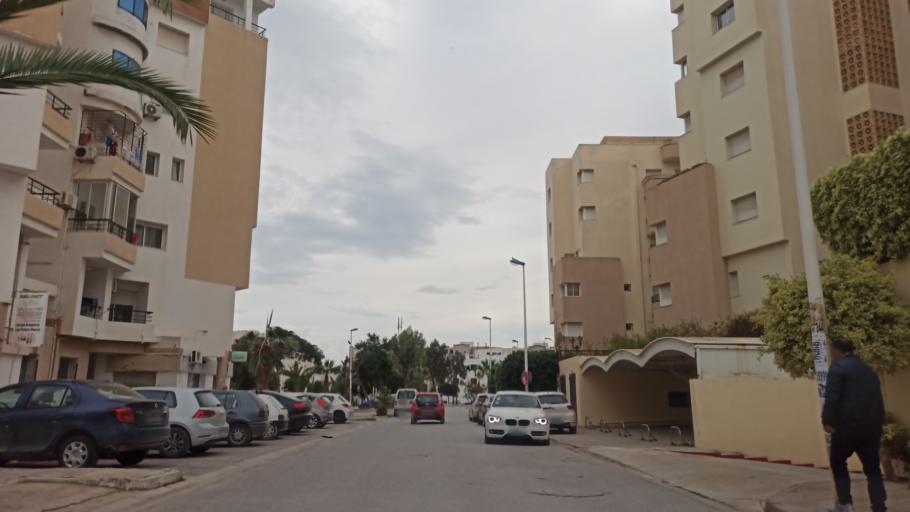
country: TN
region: Tunis
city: La Goulette
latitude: 36.8595
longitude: 10.2650
